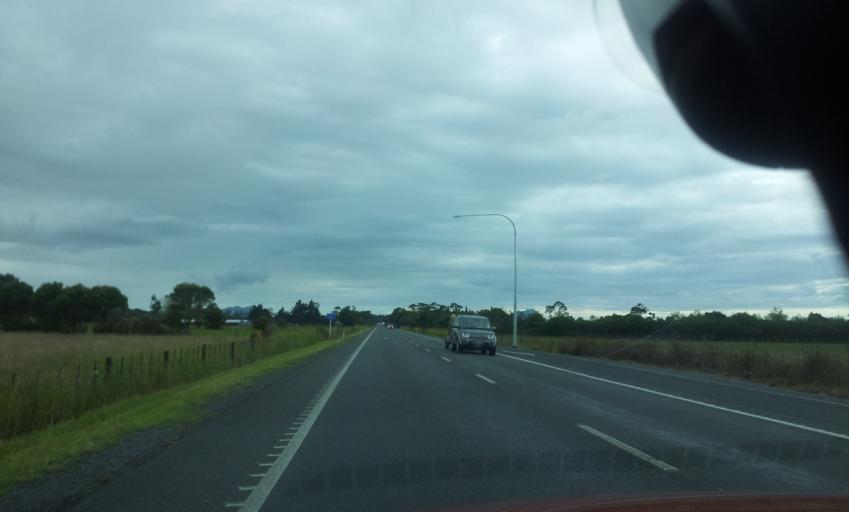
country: NZ
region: Northland
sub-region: Whangarei
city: Ruakaka
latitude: -35.9773
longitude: 174.4360
